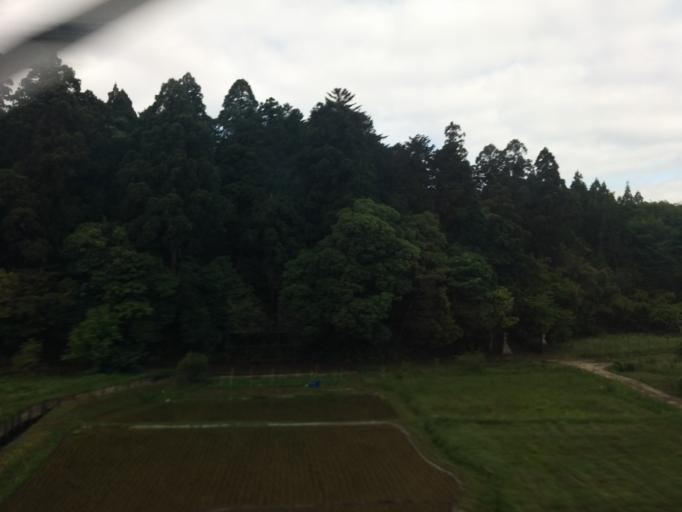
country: JP
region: Shiga Prefecture
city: Hikone
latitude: 35.2681
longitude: 136.2791
